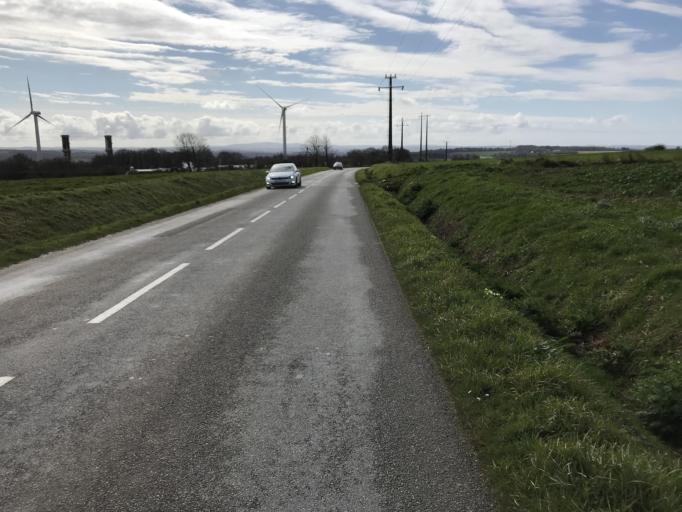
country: FR
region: Brittany
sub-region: Departement du Finistere
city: Dirinon
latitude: 48.3949
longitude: -4.2651
